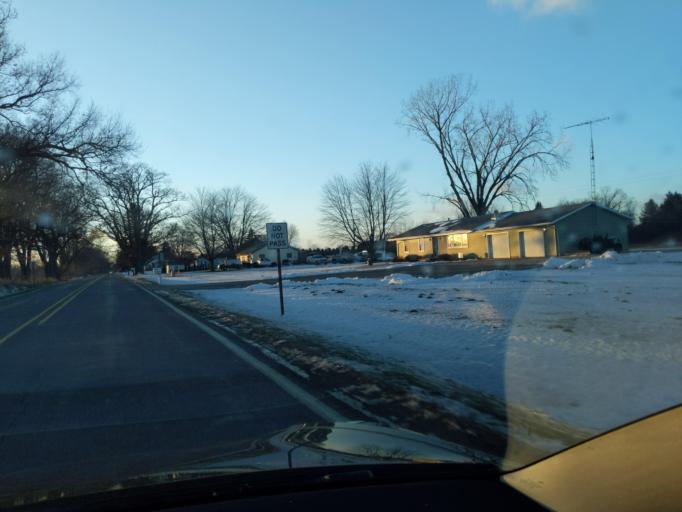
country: US
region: Michigan
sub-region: Ingham County
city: Stockbridge
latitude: 42.4540
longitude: -84.1979
